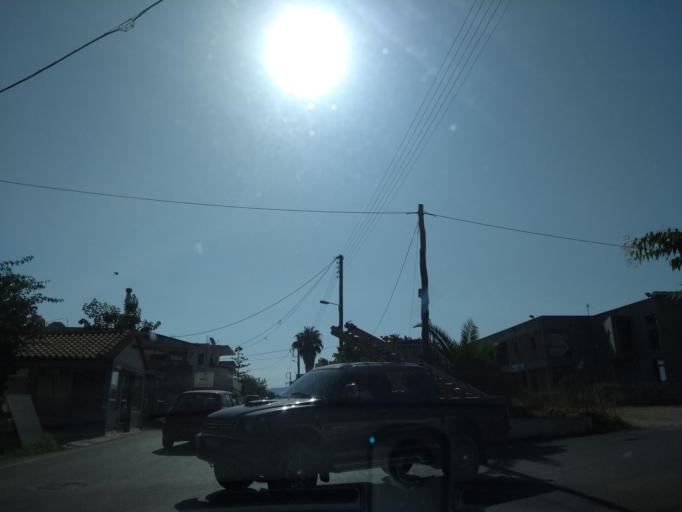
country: GR
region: Crete
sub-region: Nomos Chanias
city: Georgioupolis
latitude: 35.3477
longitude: 24.2977
